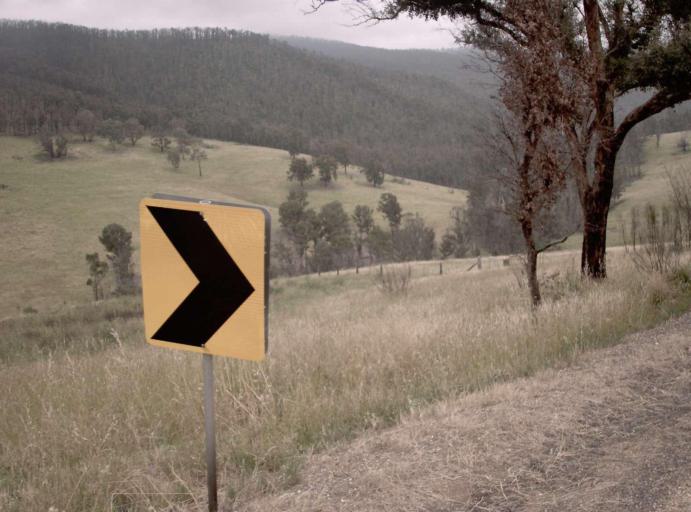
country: AU
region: Victoria
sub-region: Wellington
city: Heyfield
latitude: -37.8304
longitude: 146.6774
